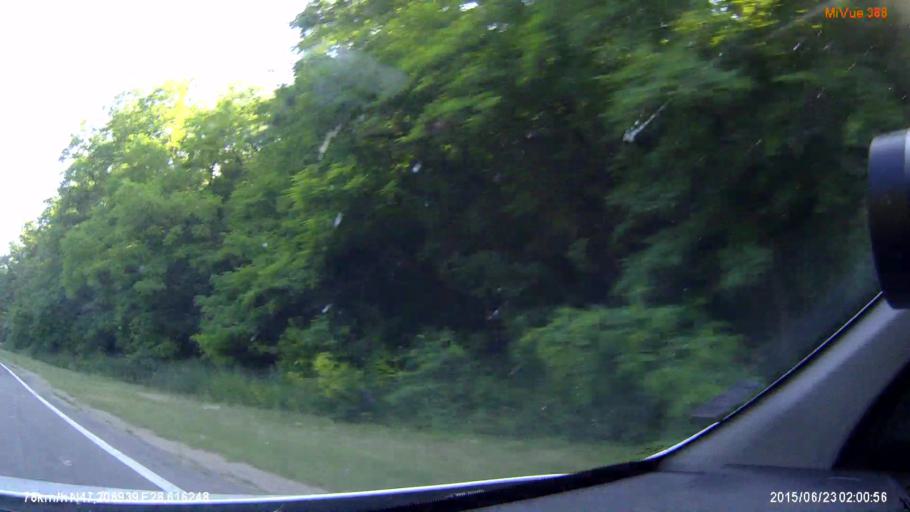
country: MD
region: Straseni
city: Straseni
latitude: 47.2073
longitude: 28.6162
